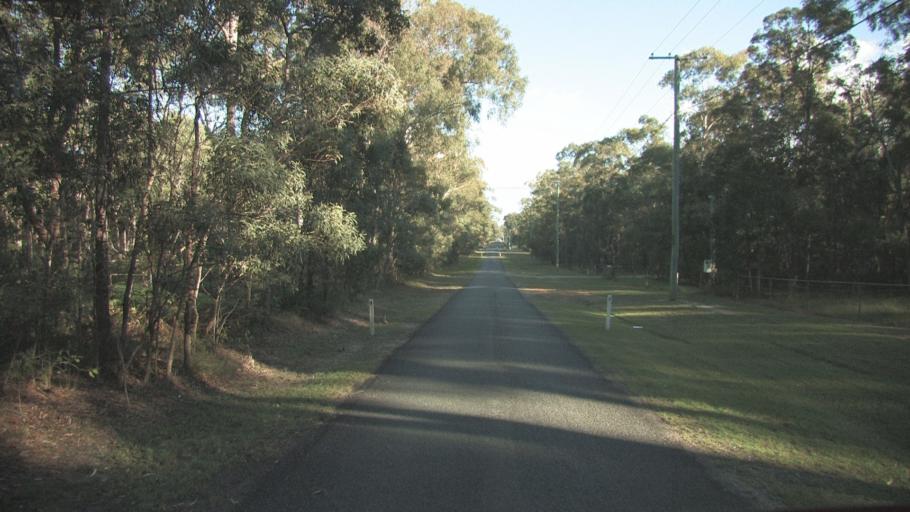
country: AU
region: Queensland
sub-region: Gold Coast
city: Yatala
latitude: -27.6662
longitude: 153.2449
